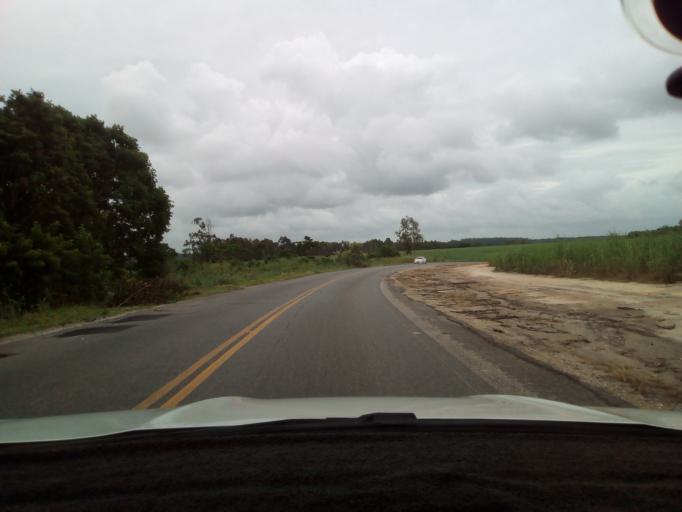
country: BR
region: Paraiba
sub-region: Pedras De Fogo
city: Pedras de Fogo
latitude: -7.3632
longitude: -35.0357
